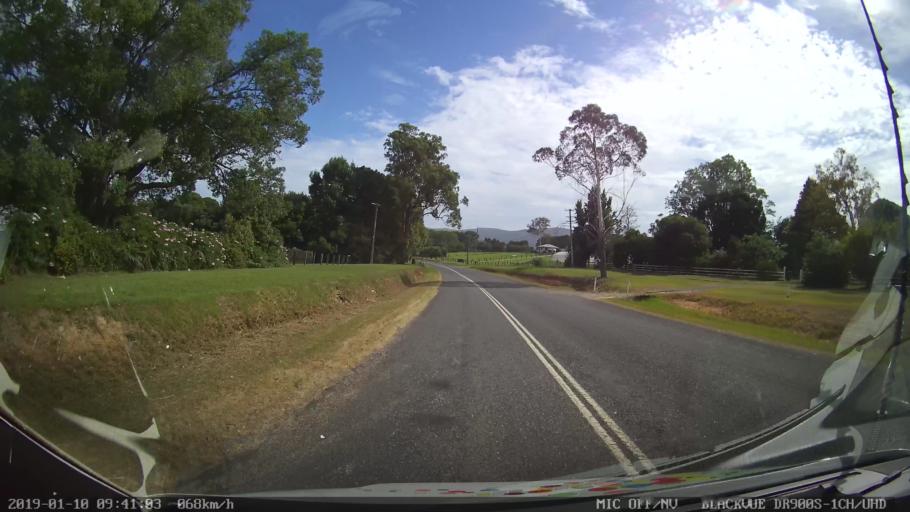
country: AU
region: New South Wales
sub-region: Coffs Harbour
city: Nana Glen
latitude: -30.1453
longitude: 153.0070
